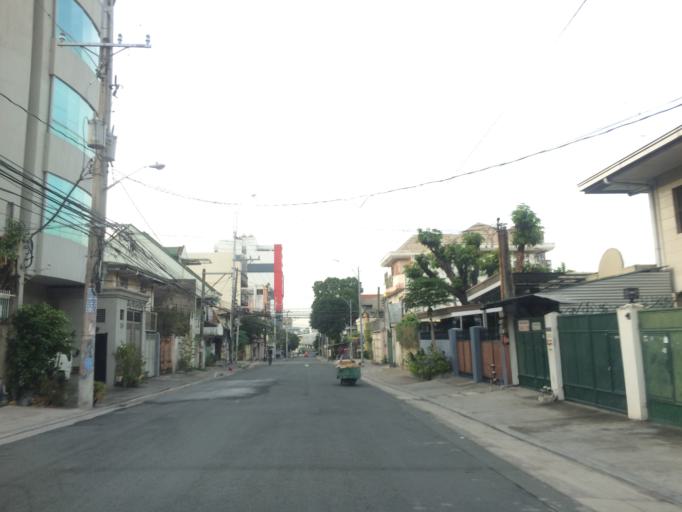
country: PH
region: Calabarzon
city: Del Monte
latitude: 14.6363
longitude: 121.0037
